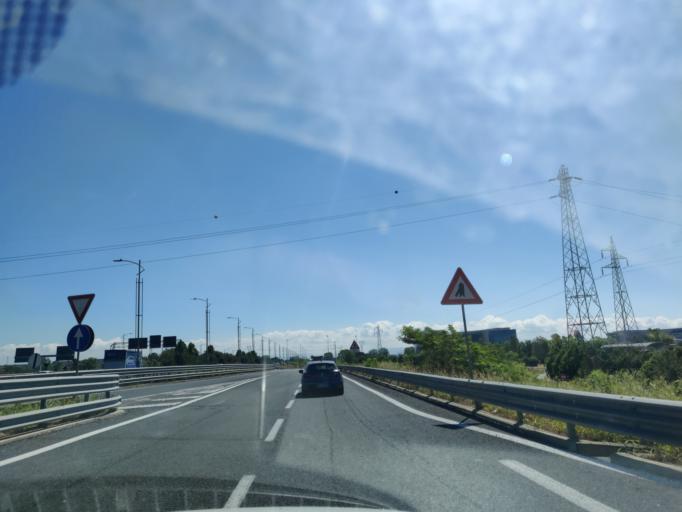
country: IT
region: Latium
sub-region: Citta metropolitana di Roma Capitale
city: Npp 23 (Parco Leonardo)
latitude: 41.8121
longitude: 12.3252
